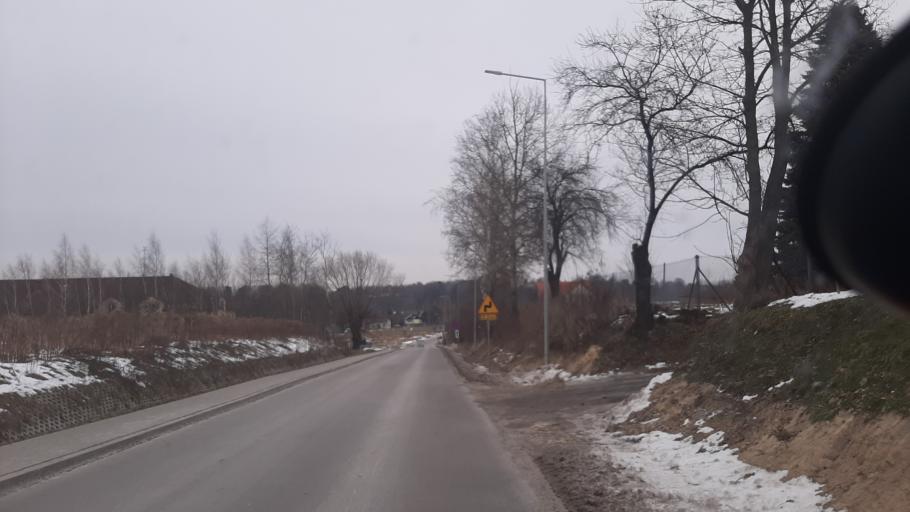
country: PL
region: Lublin Voivodeship
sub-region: Powiat lubelski
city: Jakubowice Murowane
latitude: 51.2984
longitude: 22.6327
